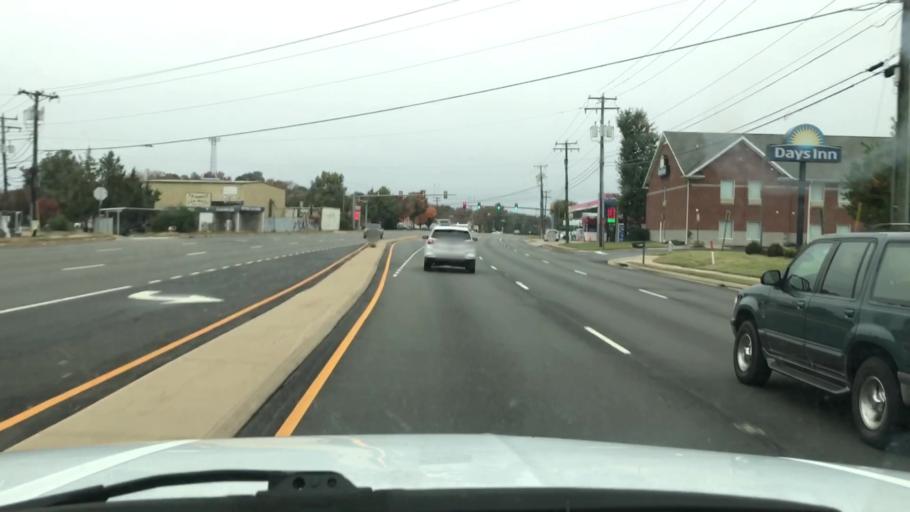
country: US
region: Virginia
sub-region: Henrico County
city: Chamberlayne
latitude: 37.6406
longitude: -77.4599
